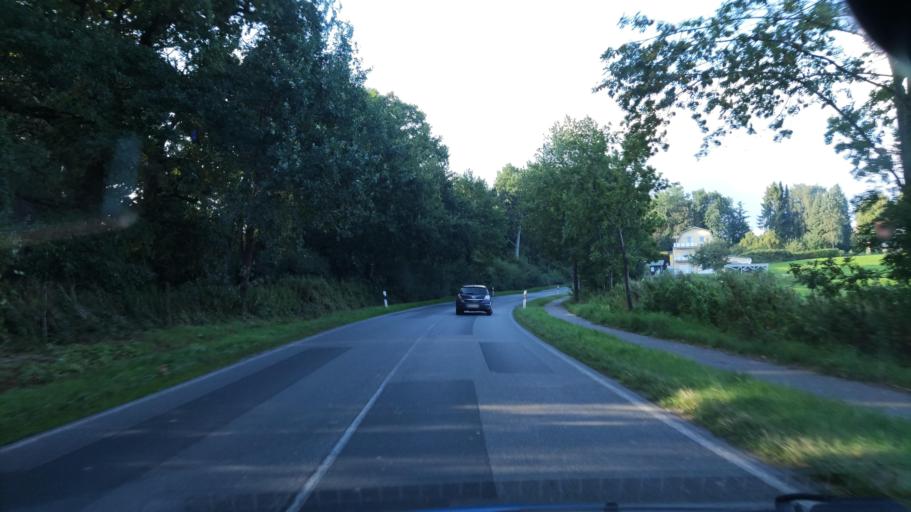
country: DE
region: Schleswig-Holstein
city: Ahrensbok
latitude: 53.9977
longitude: 10.5779
